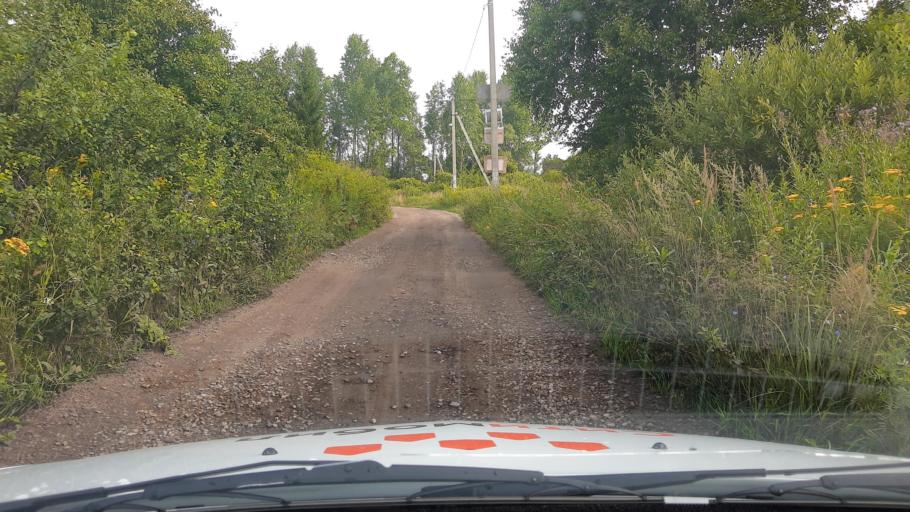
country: RU
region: Bashkortostan
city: Kabakovo
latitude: 54.7286
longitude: 56.1945
